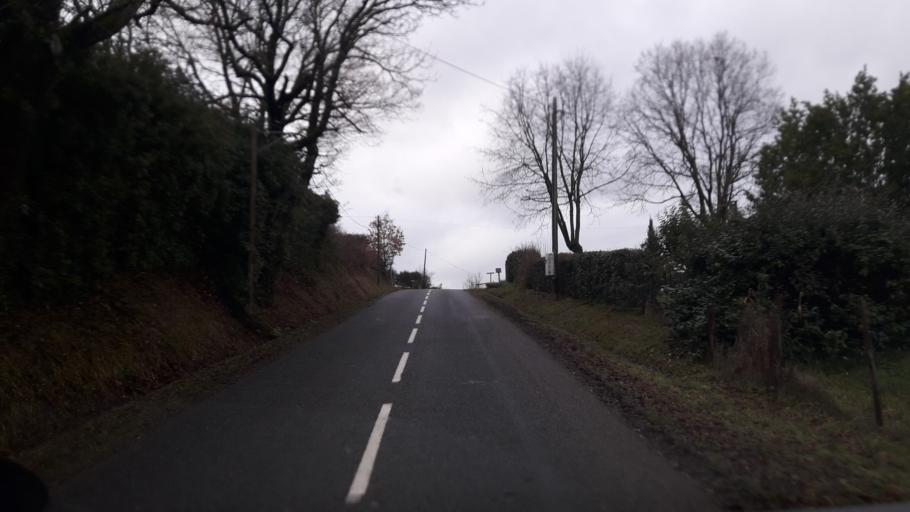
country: FR
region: Midi-Pyrenees
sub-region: Departement de la Haute-Garonne
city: Montesquieu-Volvestre
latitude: 43.2245
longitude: 1.2740
